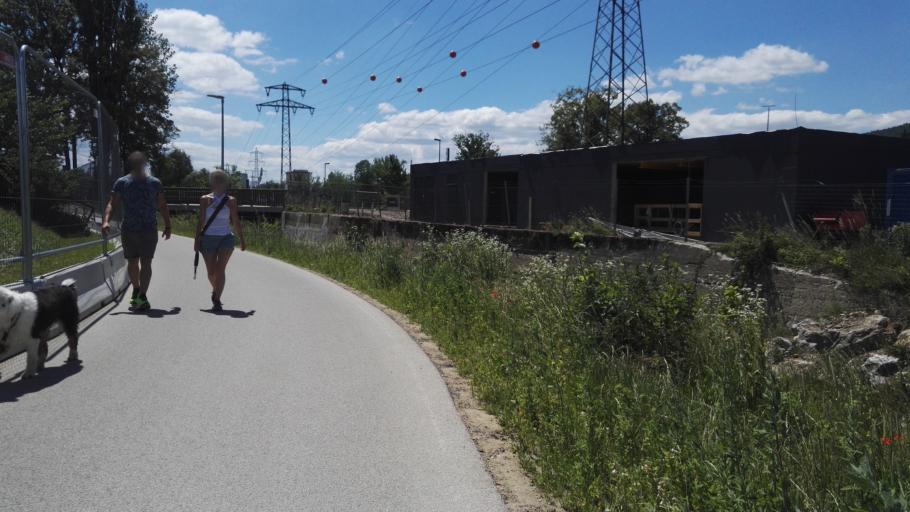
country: AT
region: Styria
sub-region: Graz Stadt
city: Goesting
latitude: 47.1024
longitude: 15.4135
